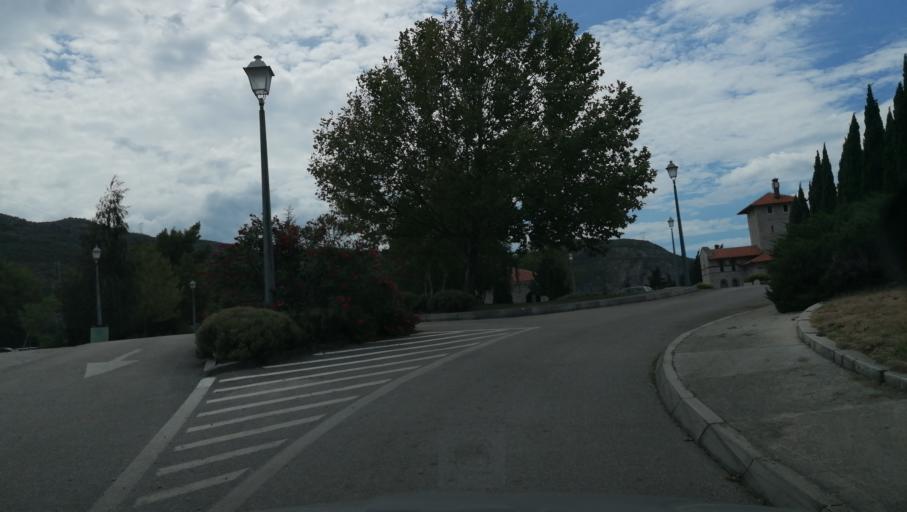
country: BA
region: Republika Srpska
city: Trebinje
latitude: 42.7110
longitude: 18.3606
